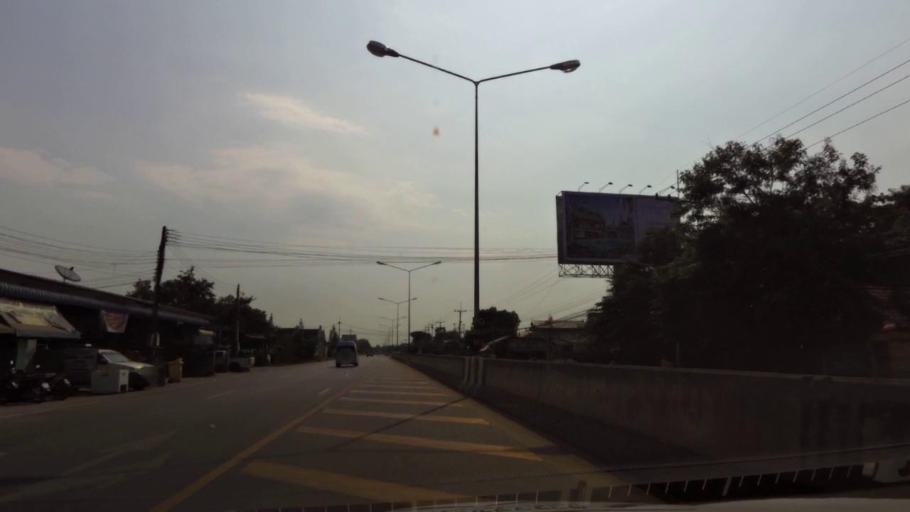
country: TH
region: Phra Nakhon Si Ayutthaya
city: Phra Nakhon Si Ayutthaya
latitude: 14.3266
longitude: 100.5760
